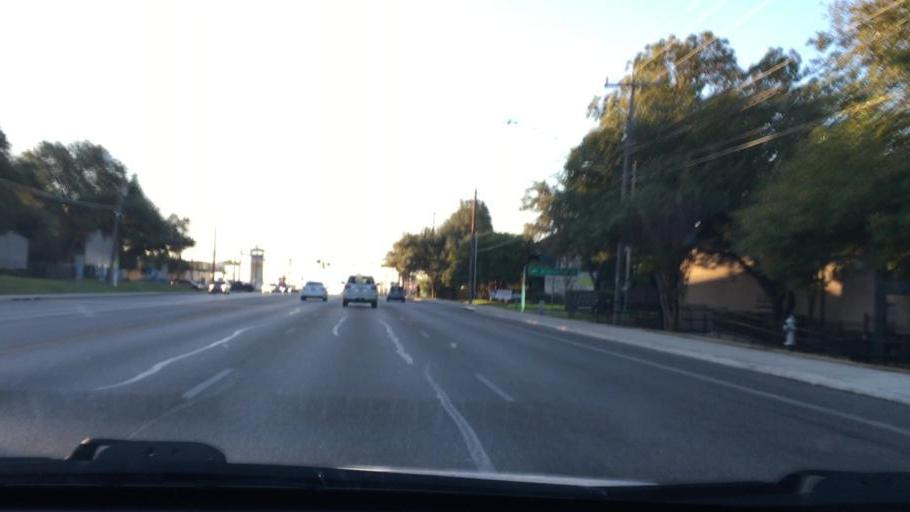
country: US
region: Texas
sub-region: Bexar County
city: Castle Hills
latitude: 29.5464
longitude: -98.5302
